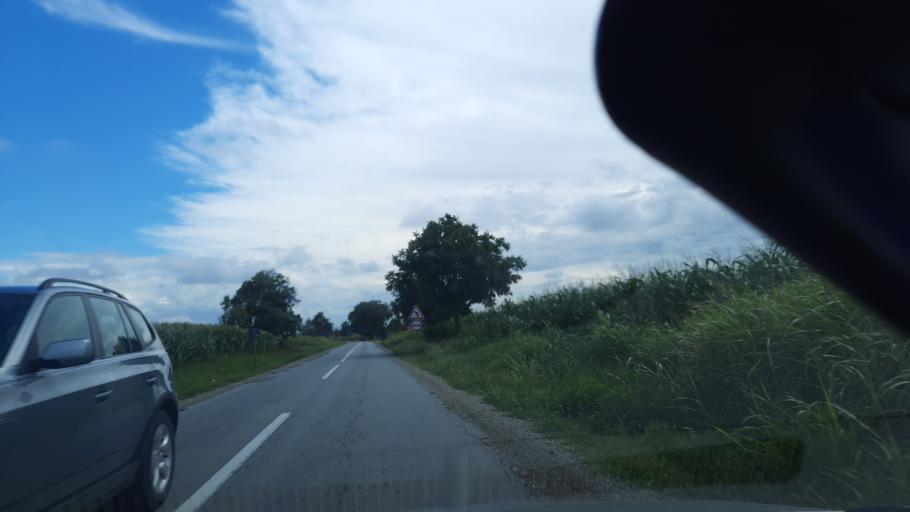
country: RS
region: Autonomna Pokrajina Vojvodina
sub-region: Sremski Okrug
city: Sremska Mitrovica
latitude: 45.1065
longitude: 19.5674
